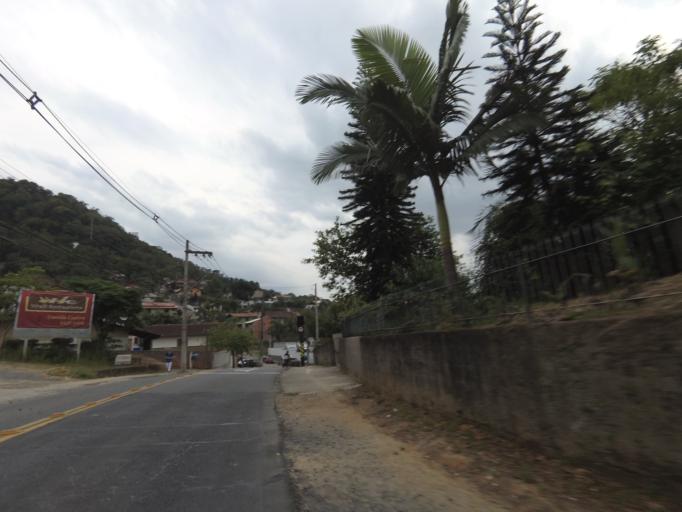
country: BR
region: Santa Catarina
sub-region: Blumenau
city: Blumenau
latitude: -26.8743
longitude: -49.0510
